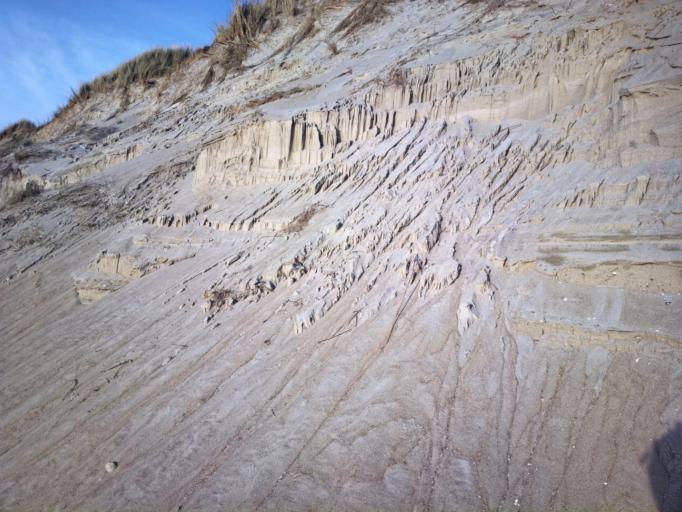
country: NL
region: North Holland
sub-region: Gemeente Den Helder
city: Den Helder
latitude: 53.0086
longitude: 4.7122
